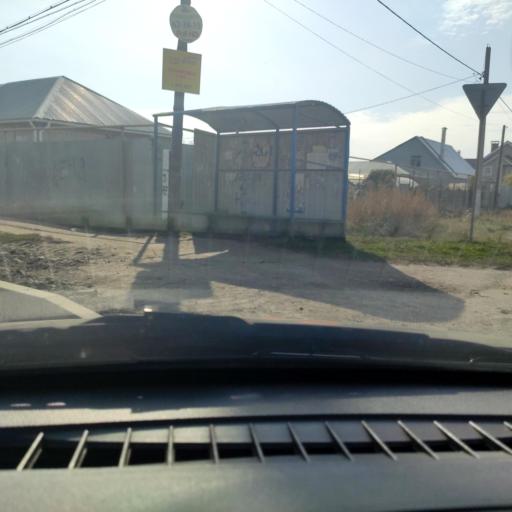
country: RU
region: Samara
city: Podstepki
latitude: 53.5113
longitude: 49.2359
